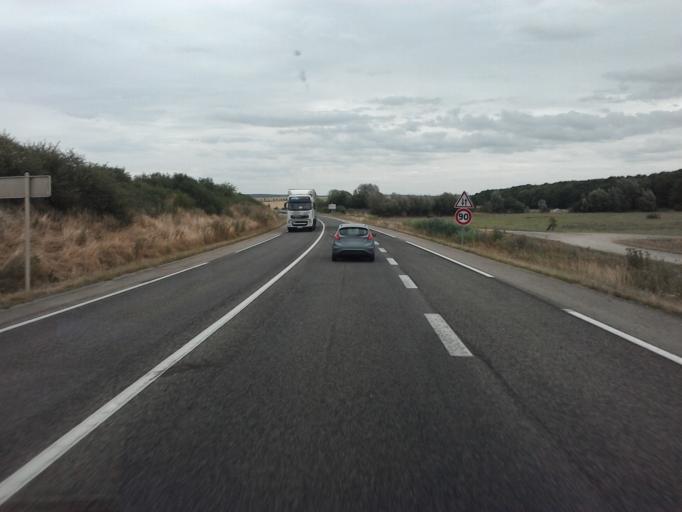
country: FR
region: Lorraine
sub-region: Departement de Meurthe-et-Moselle
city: Bainville-sur-Madon
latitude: 48.5782
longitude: 6.0563
